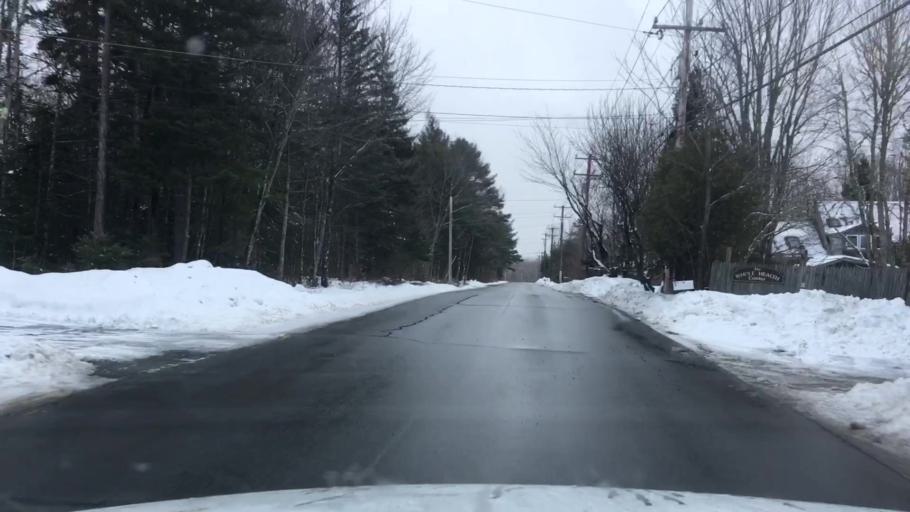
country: US
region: Maine
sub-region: Hancock County
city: Trenton
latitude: 44.4105
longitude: -68.3329
